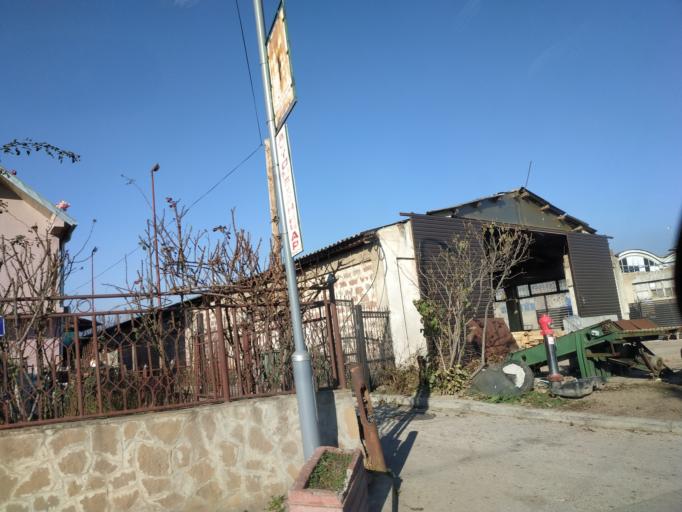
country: RS
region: Central Serbia
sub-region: Nisavski Okrug
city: Aleksinac
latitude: 43.5343
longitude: 21.7056
